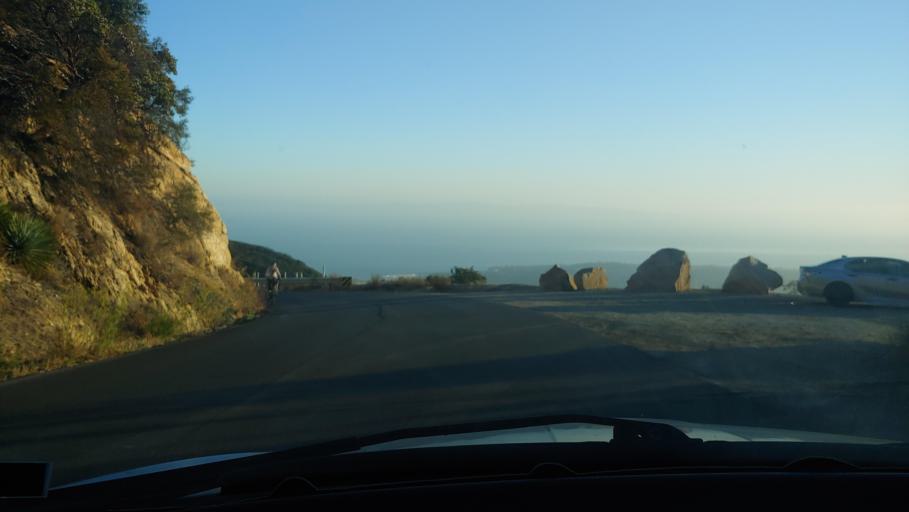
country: US
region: California
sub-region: Santa Barbara County
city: Mission Canyon
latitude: 34.4791
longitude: -119.6812
